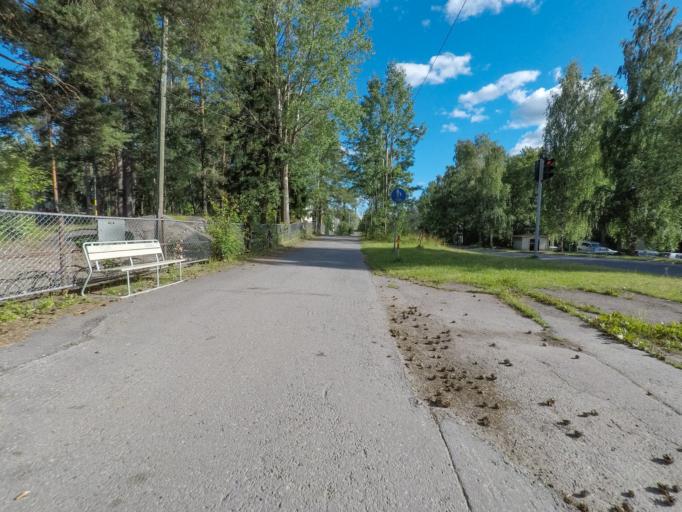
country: FI
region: South Karelia
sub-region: Lappeenranta
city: Lappeenranta
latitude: 61.0811
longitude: 28.1489
